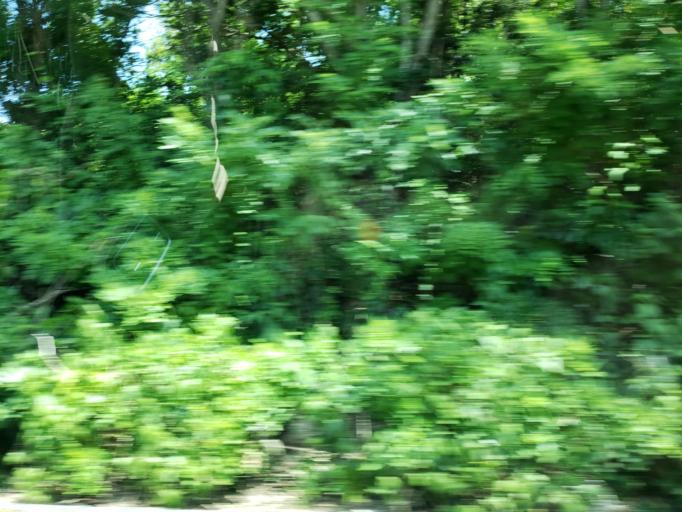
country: ID
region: Bali
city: Kangin
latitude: -8.8431
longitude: 115.1386
